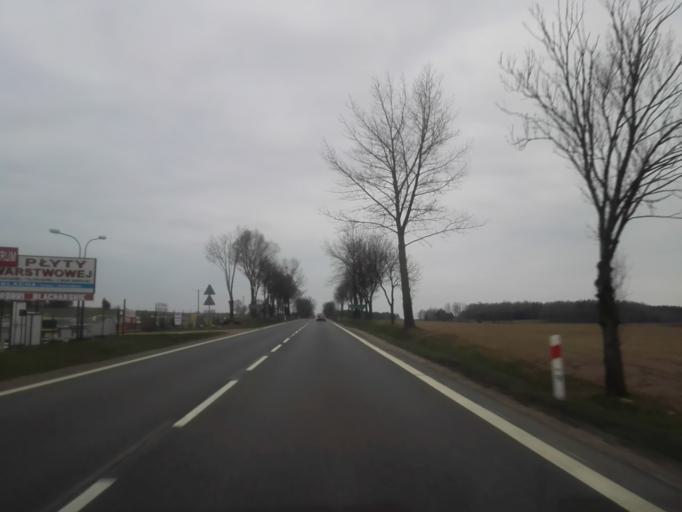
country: PL
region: Podlasie
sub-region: Powiat kolnenski
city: Stawiski
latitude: 53.4582
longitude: 22.1937
